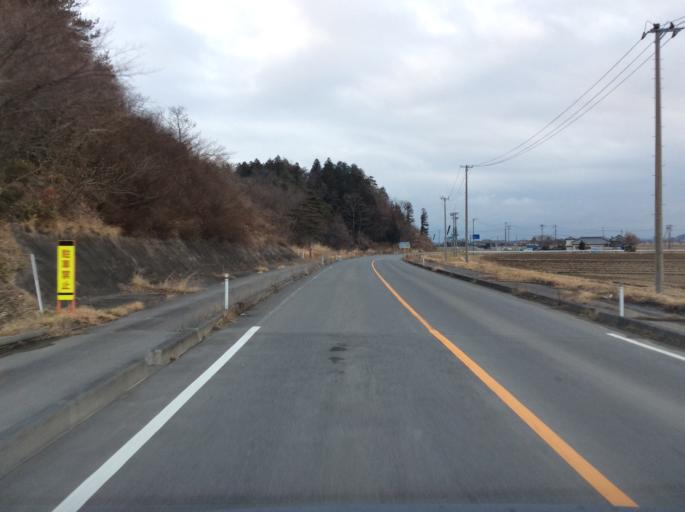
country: JP
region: Fukushima
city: Iwaki
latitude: 37.1178
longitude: 140.9551
